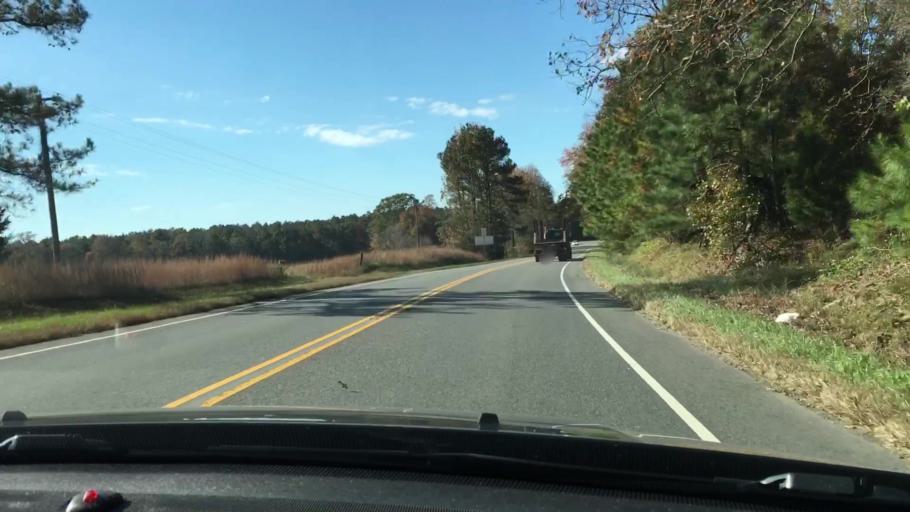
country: US
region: Virginia
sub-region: King William County
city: Central Garage
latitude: 37.7888
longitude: -77.1926
